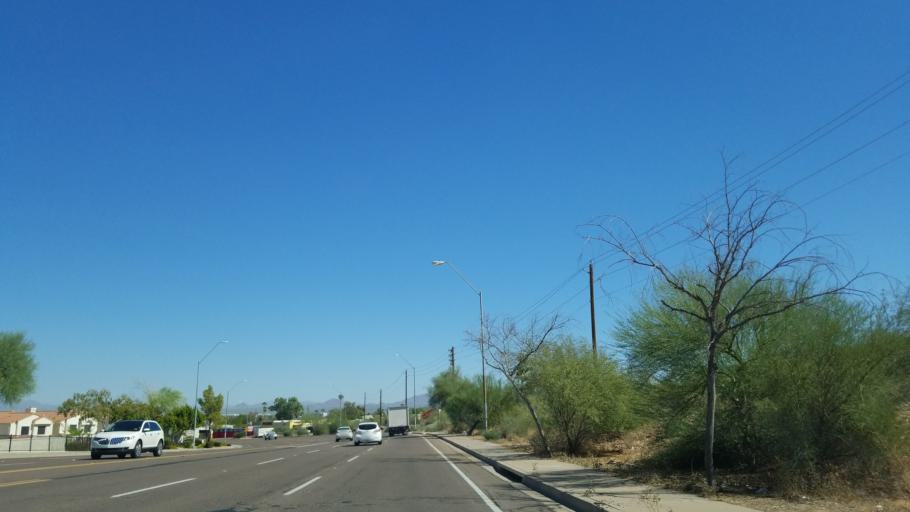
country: US
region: Arizona
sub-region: Maricopa County
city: Paradise Valley
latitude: 33.6107
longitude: -112.0355
